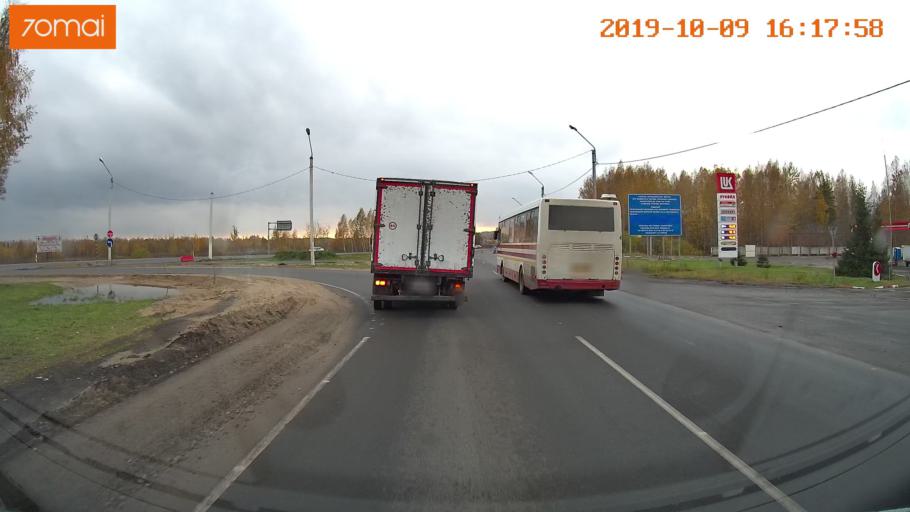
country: RU
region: Kostroma
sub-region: Kostromskoy Rayon
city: Kostroma
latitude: 57.7272
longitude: 40.8951
